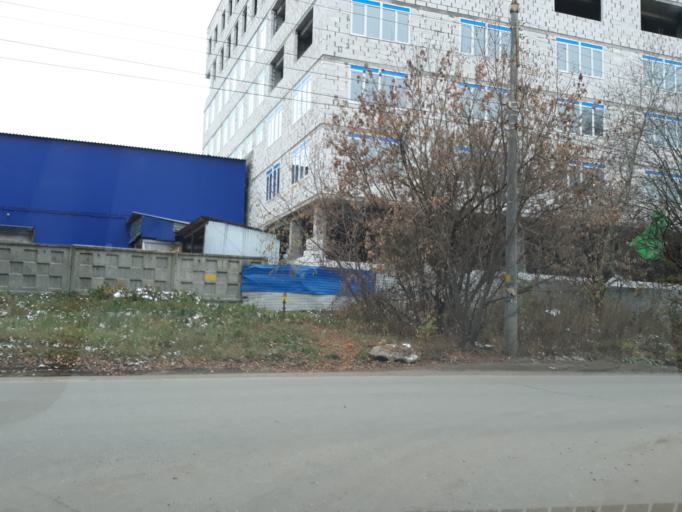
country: RU
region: Nizjnij Novgorod
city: Nizhniy Novgorod
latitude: 56.2453
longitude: 43.9731
